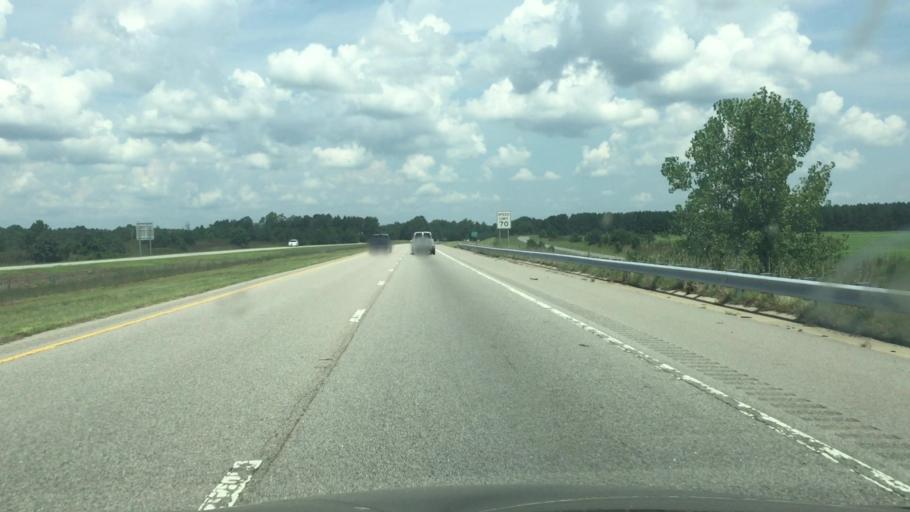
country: US
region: North Carolina
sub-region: Richmond County
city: Ellerbe
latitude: 35.1571
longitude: -79.7156
